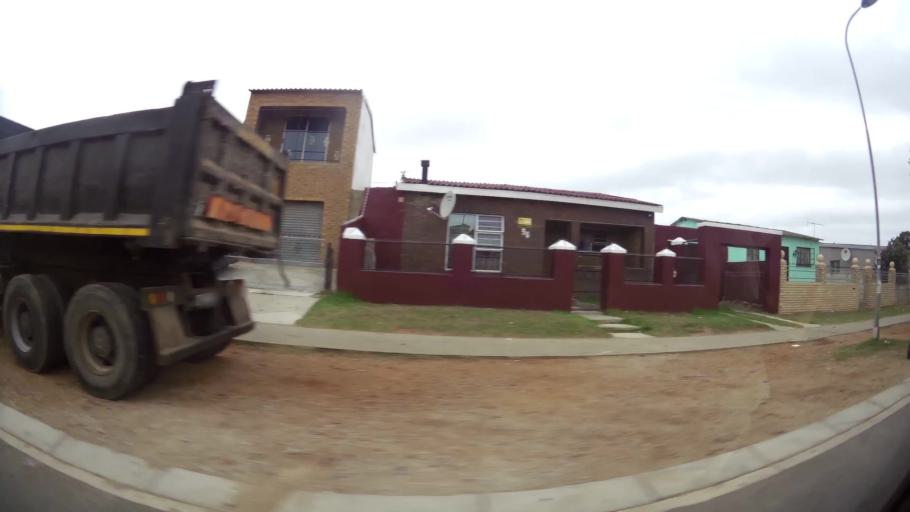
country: ZA
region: Eastern Cape
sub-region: Nelson Mandela Bay Metropolitan Municipality
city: Port Elizabeth
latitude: -33.9115
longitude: 25.5483
